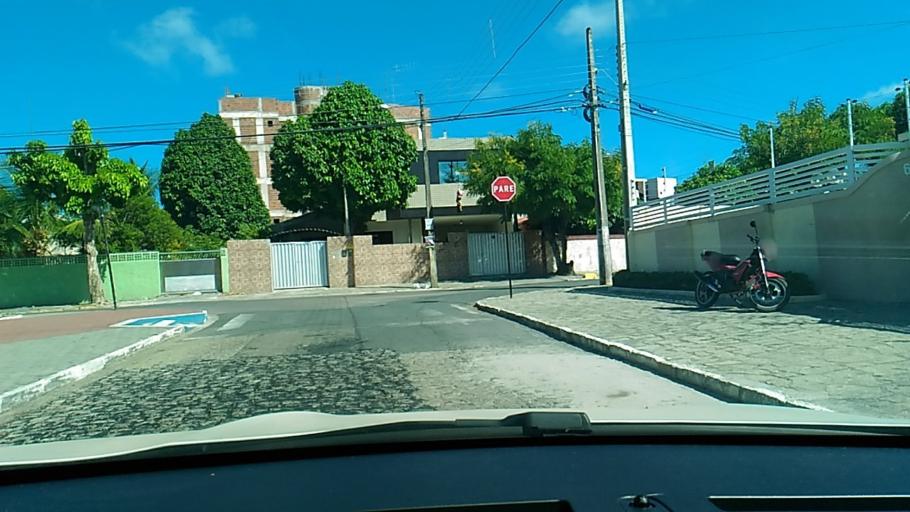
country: BR
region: Paraiba
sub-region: Joao Pessoa
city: Joao Pessoa
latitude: -7.1484
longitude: -34.8385
